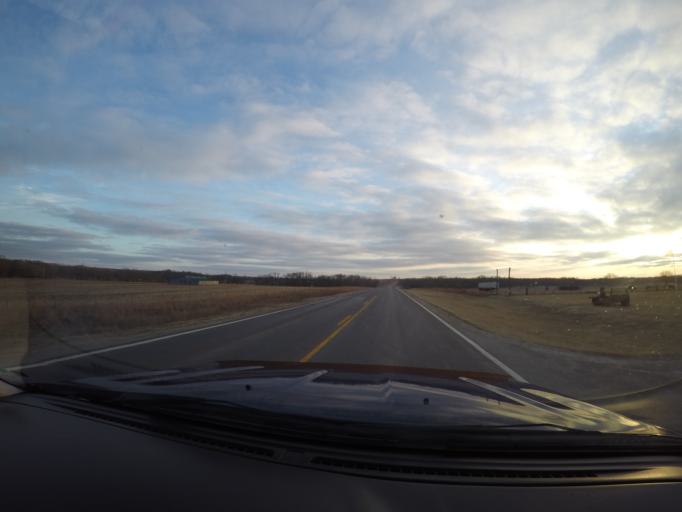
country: US
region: Kansas
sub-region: Morris County
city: Council Grove
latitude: 38.6048
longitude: -96.4992
